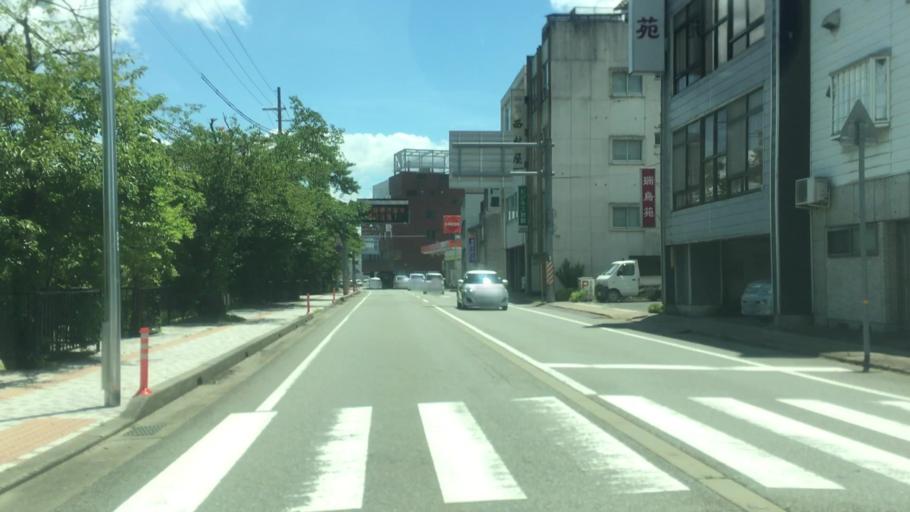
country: JP
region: Hyogo
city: Toyooka
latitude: 35.5418
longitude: 134.8244
